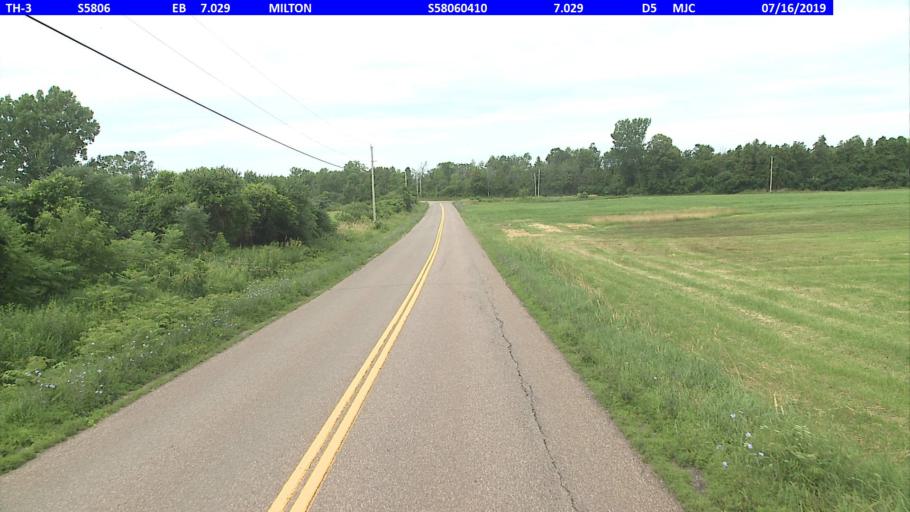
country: US
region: Vermont
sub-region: Chittenden County
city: Milton
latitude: 44.7003
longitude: -73.2038
